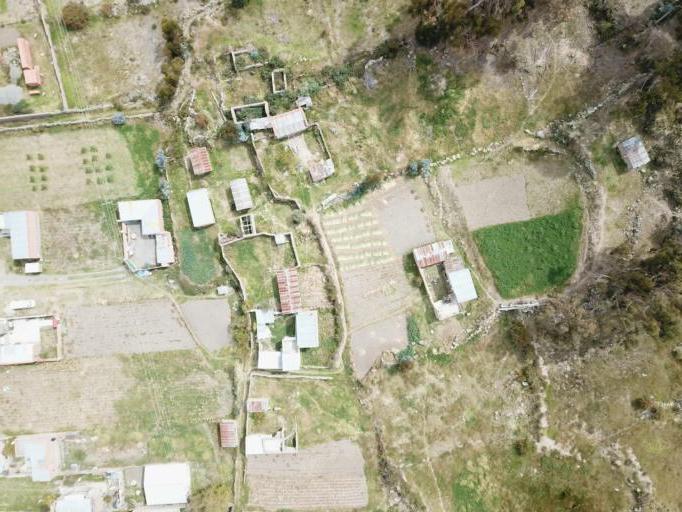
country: BO
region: La Paz
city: Achacachi
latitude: -16.0508
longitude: -68.8175
